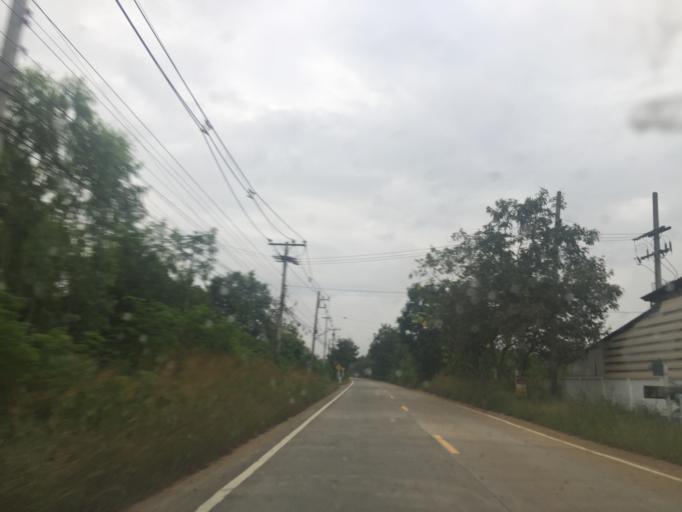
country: TH
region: Lamphun
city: Ban Thi
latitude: 18.6247
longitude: 99.0747
